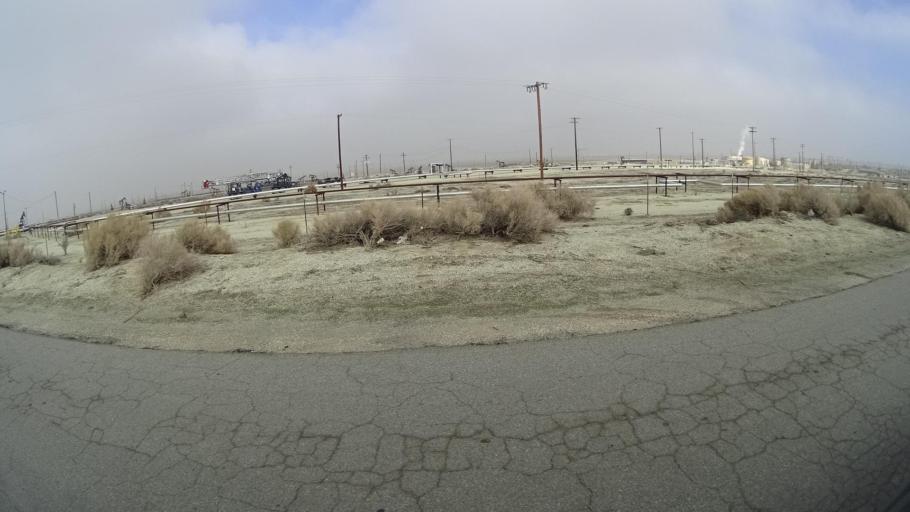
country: US
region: California
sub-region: Kern County
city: Maricopa
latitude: 35.0323
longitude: -119.3478
